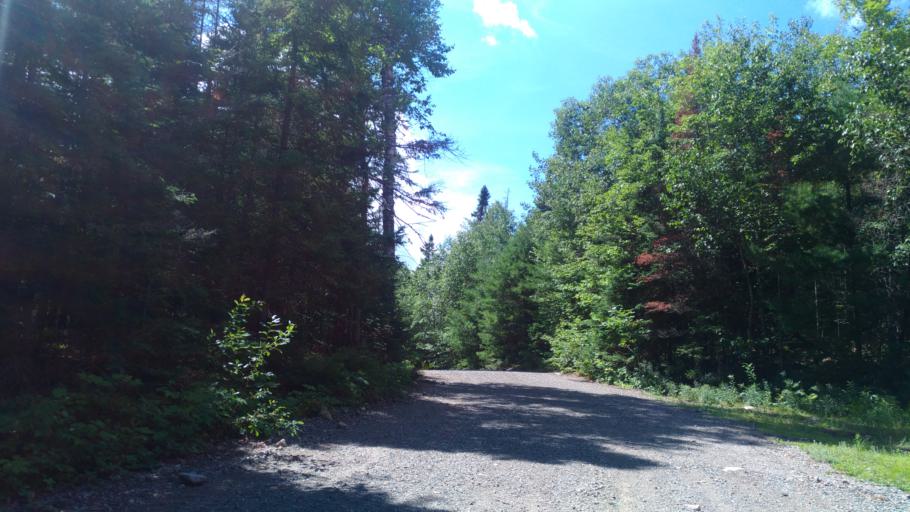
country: CA
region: Ontario
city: Rayside-Balfour
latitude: 46.5925
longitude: -81.5496
